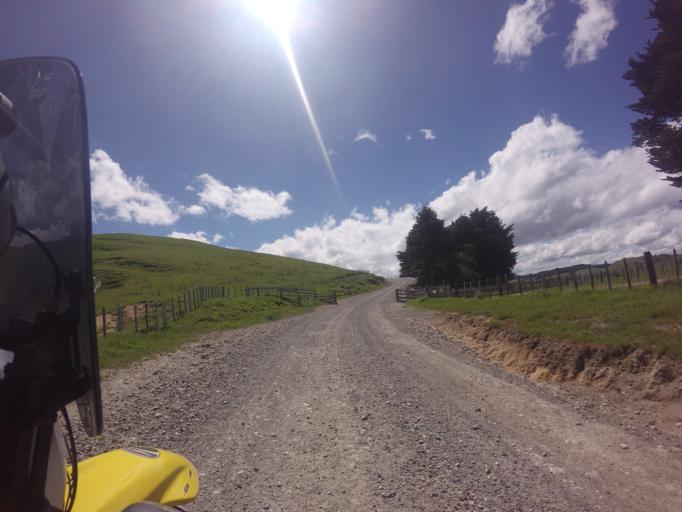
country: NZ
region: Hawke's Bay
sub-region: Wairoa District
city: Wairoa
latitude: -38.9619
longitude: 177.7153
